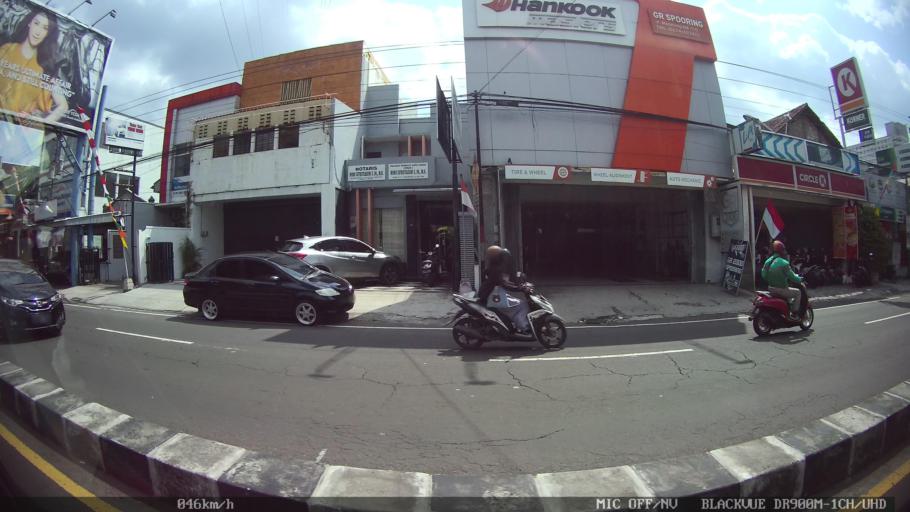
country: ID
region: Daerah Istimewa Yogyakarta
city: Melati
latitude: -7.7552
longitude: 110.3619
